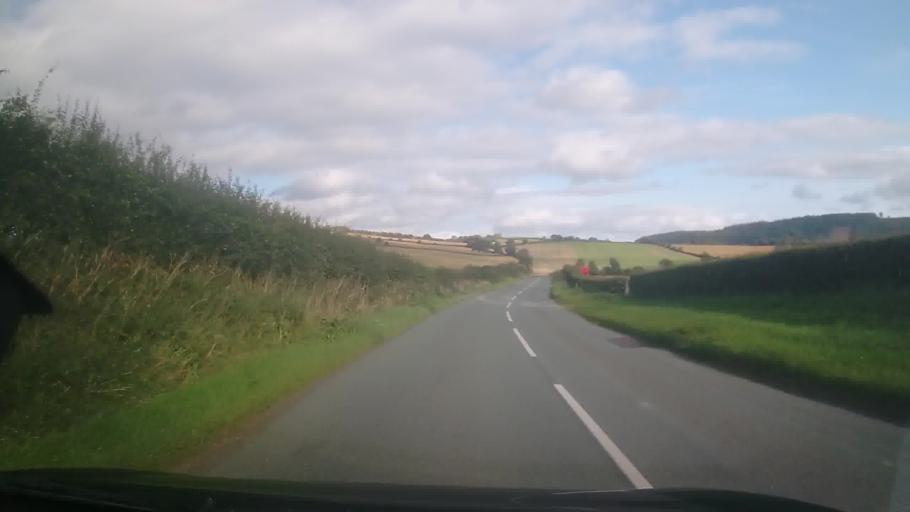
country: GB
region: England
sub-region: Shropshire
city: Lydham
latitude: 52.4680
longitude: -2.9405
